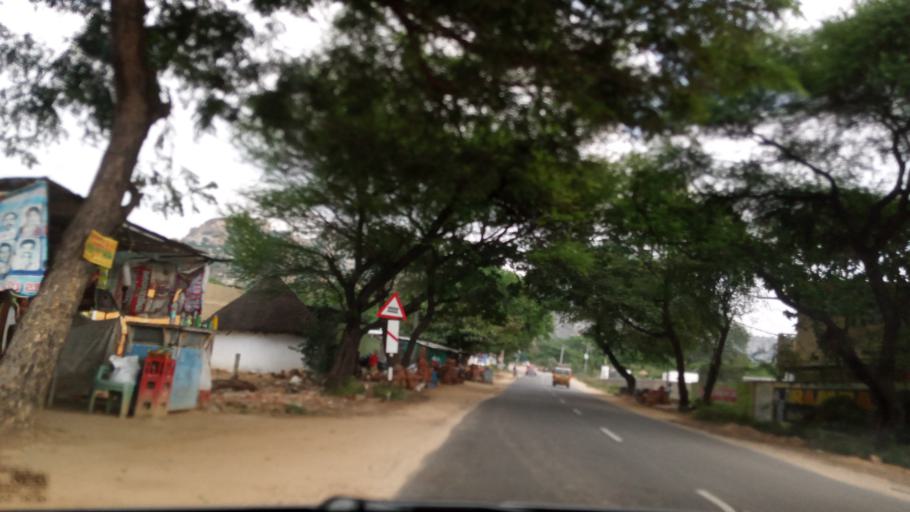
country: IN
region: Andhra Pradesh
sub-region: Chittoor
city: Madanapalle
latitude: 13.6434
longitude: 78.5643
